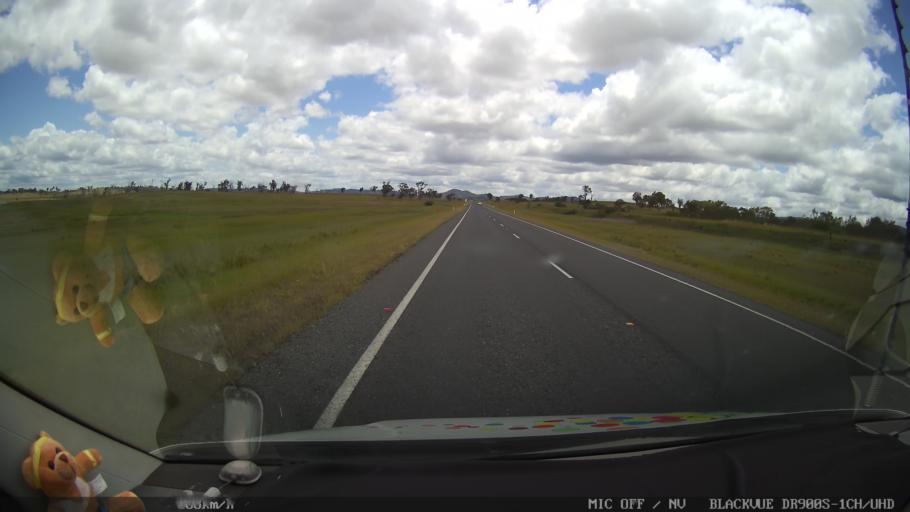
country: AU
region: New South Wales
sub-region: Glen Innes Severn
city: Glen Innes
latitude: -29.4097
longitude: 151.8684
